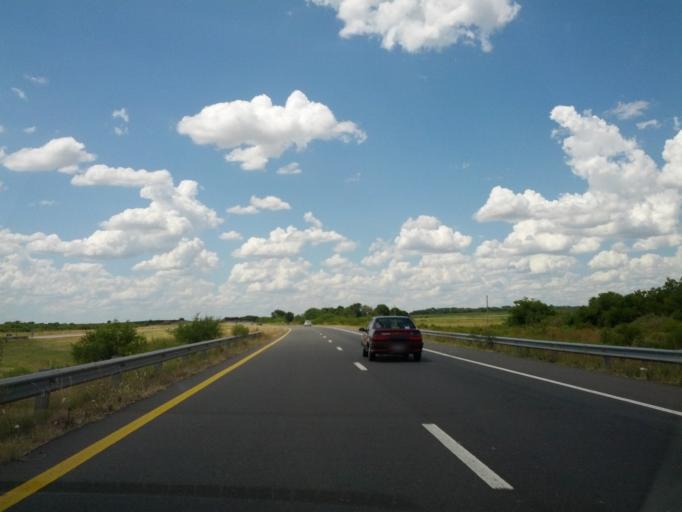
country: AR
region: Entre Rios
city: Colonia Elia
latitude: -32.7489
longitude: -58.4819
